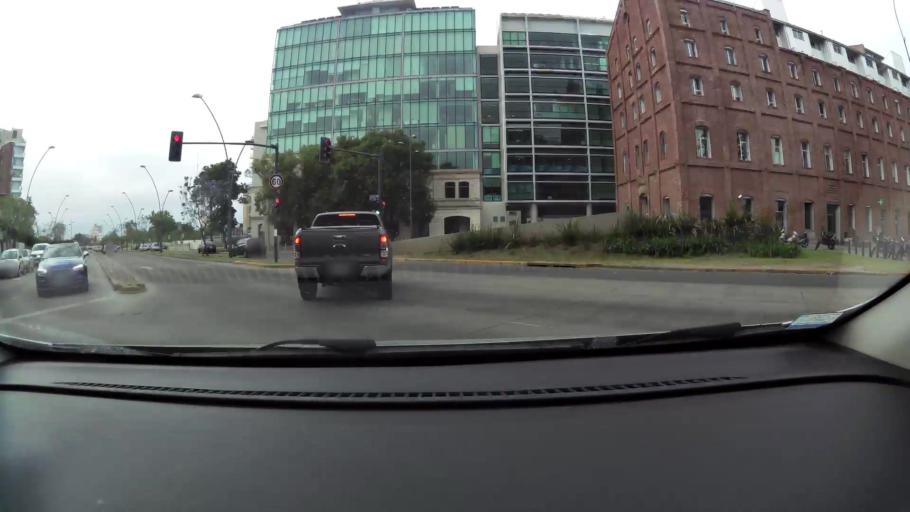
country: AR
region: Santa Fe
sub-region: Departamento de Rosario
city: Rosario
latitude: -32.9234
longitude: -60.6656
